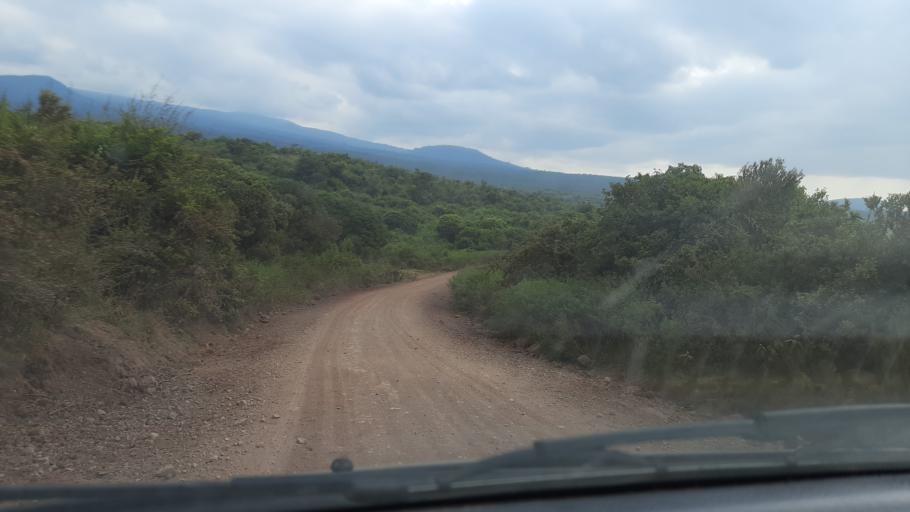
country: TZ
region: Kilimanjaro
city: Moshi
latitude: -2.8583
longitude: 37.2696
